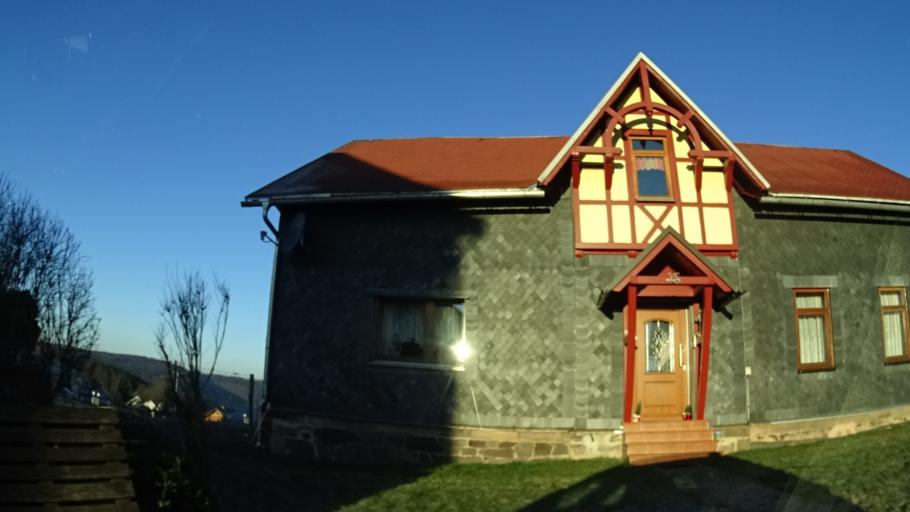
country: DE
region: Thuringia
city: Judenbach
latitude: 50.3970
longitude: 11.2220
